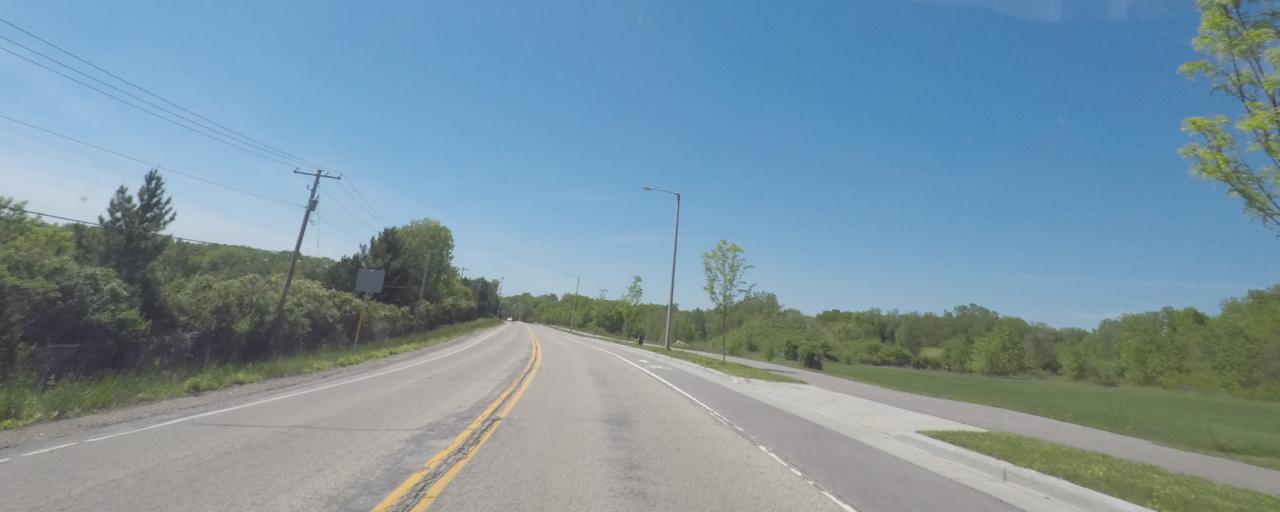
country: US
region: Wisconsin
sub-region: Dane County
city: Verona
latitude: 42.9774
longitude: -89.5284
